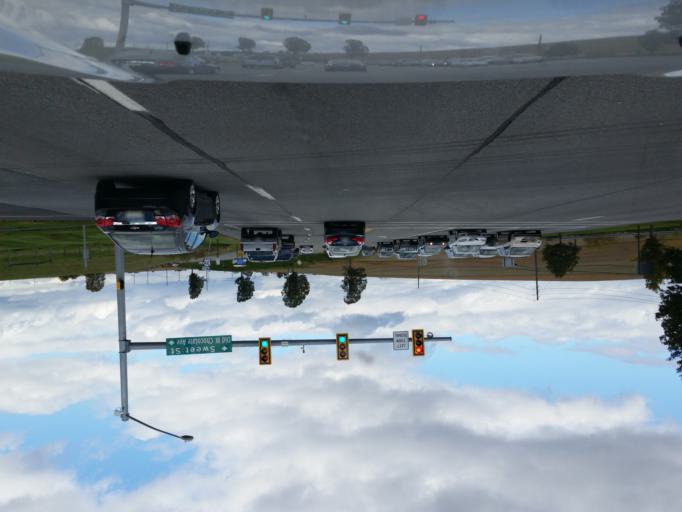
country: US
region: Pennsylvania
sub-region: Dauphin County
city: Hummelstown
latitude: 40.2724
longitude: -76.6895
